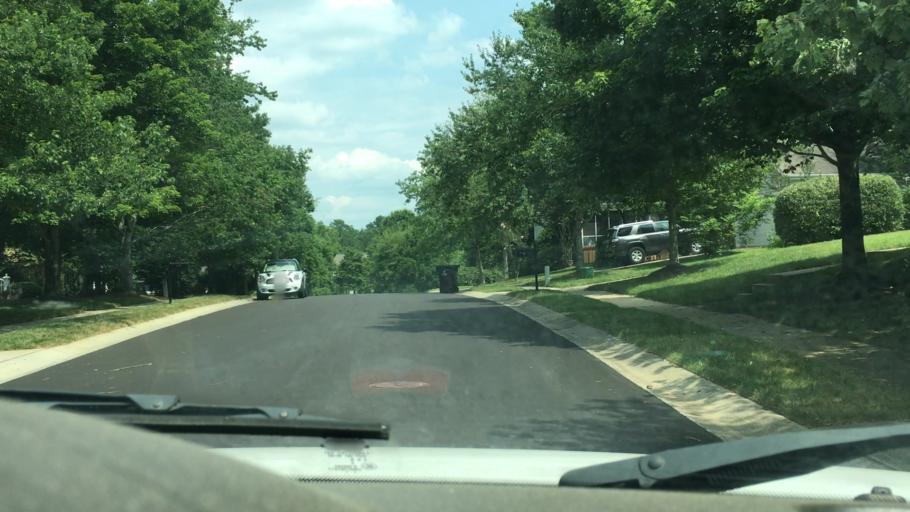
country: US
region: North Carolina
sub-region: Gaston County
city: Davidson
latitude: 35.4927
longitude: -80.8258
